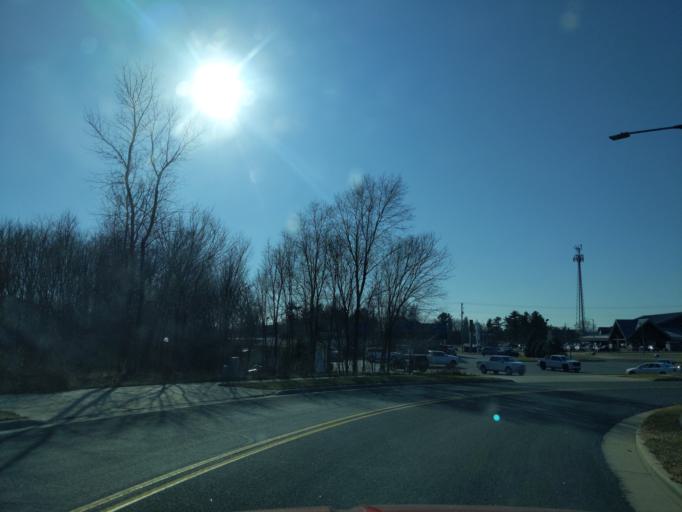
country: US
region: Wisconsin
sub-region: Waushara County
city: Wautoma
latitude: 44.0704
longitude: -89.2675
